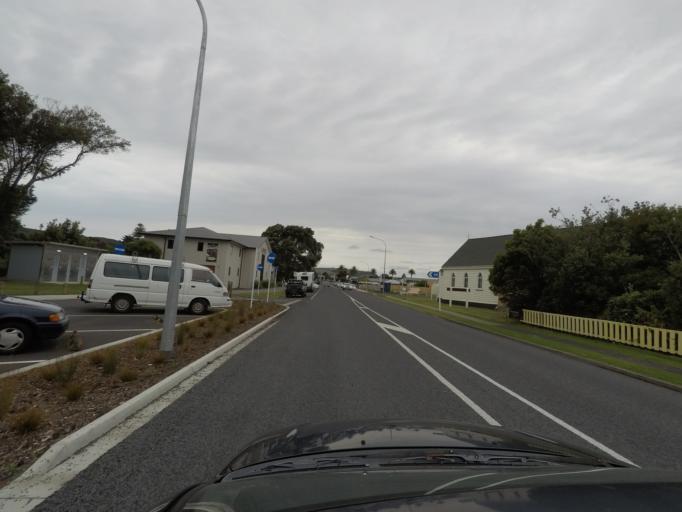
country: NZ
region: Waikato
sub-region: Waikato District
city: Raglan
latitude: -37.8025
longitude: 174.8686
